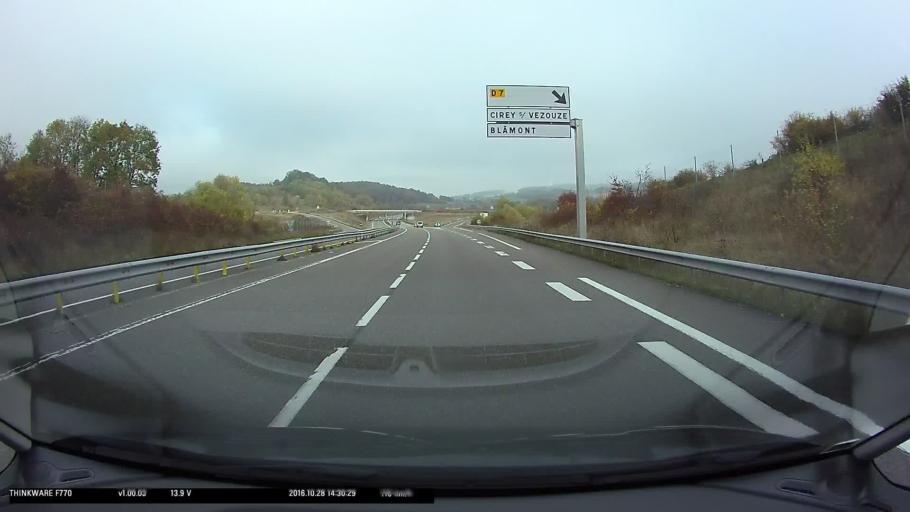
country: FR
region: Lorraine
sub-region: Departement de la Moselle
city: Lorquin
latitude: 48.6001
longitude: 6.8422
